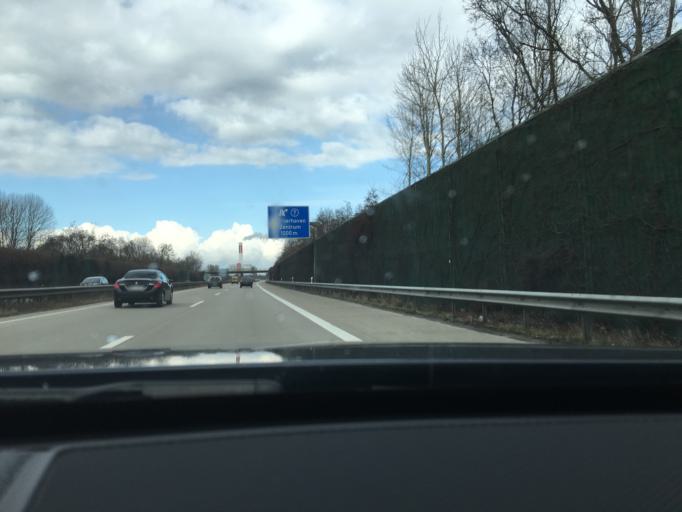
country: DE
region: Lower Saxony
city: Schiffdorf
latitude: 53.5361
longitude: 8.6208
